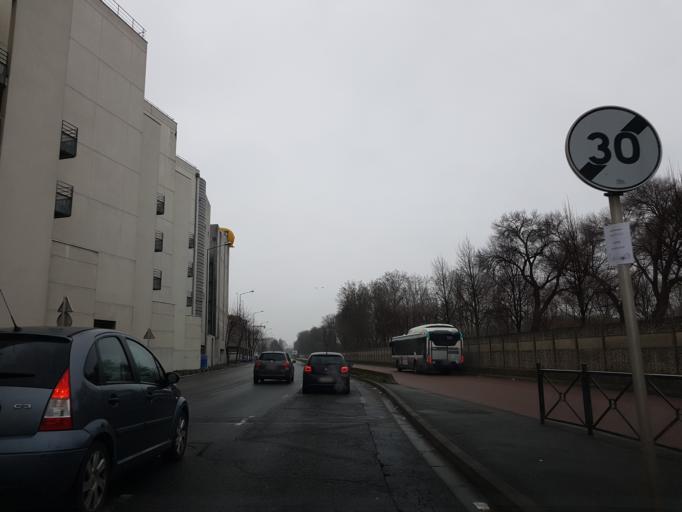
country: FR
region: Ile-de-France
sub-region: Departement du Val-de-Marne
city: Orly
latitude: 48.7566
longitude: 2.3740
